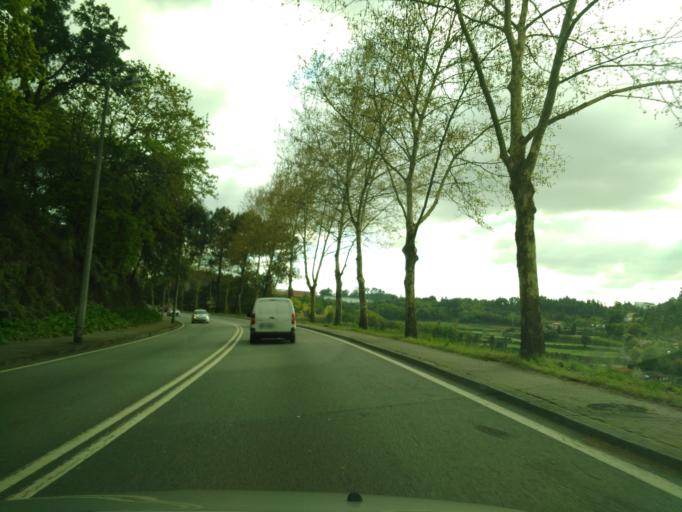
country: PT
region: Braga
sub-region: Guimaraes
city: Urgeses
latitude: 41.4275
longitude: -8.3044
